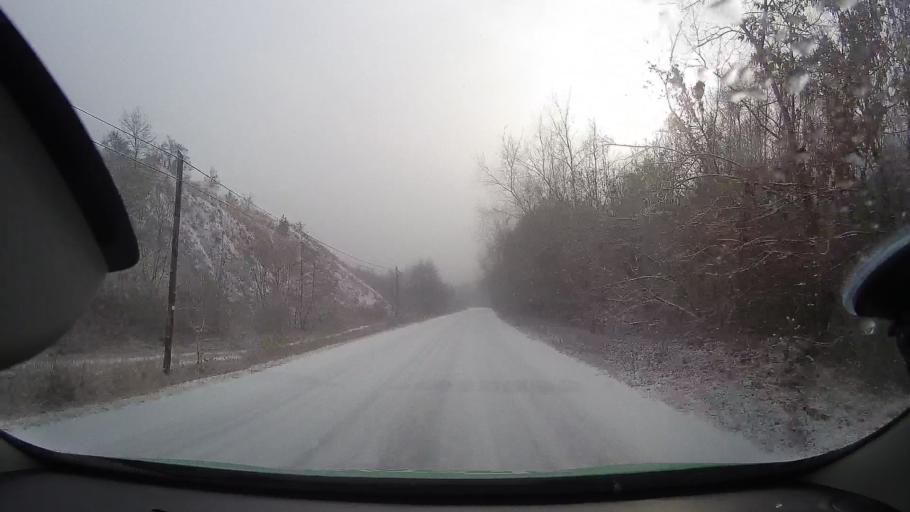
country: RO
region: Alba
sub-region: Comuna Livezile
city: Livezile
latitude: 46.3584
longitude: 23.6134
